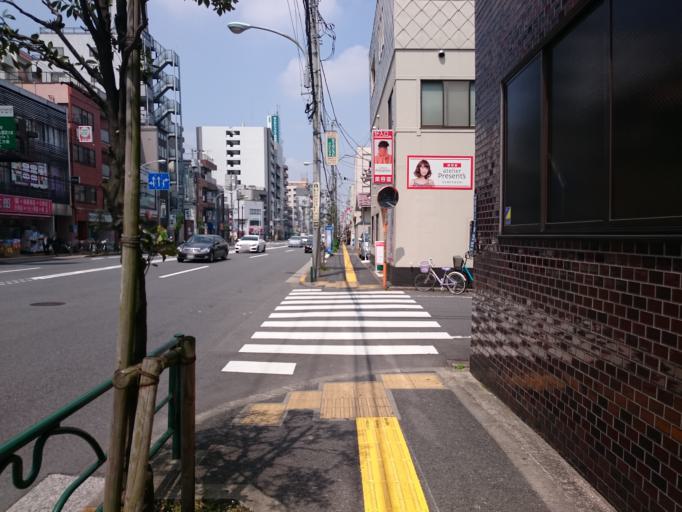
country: JP
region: Tokyo
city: Urayasu
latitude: 35.6880
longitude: 139.8158
